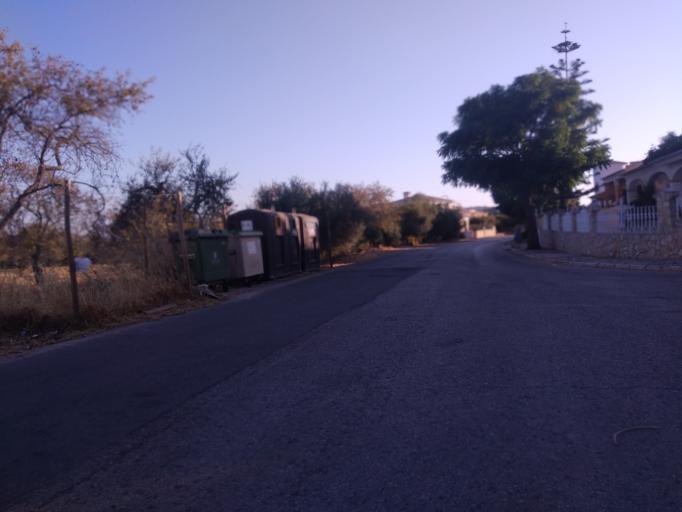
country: PT
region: Faro
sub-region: Sao Bras de Alportel
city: Sao Bras de Alportel
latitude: 37.1601
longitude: -7.8924
